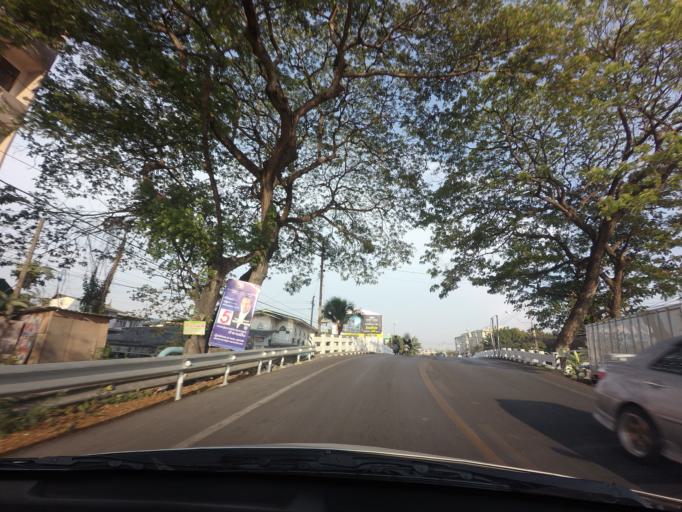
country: TH
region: Bangkok
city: Saphan Sung
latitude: 13.7403
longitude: 100.6879
